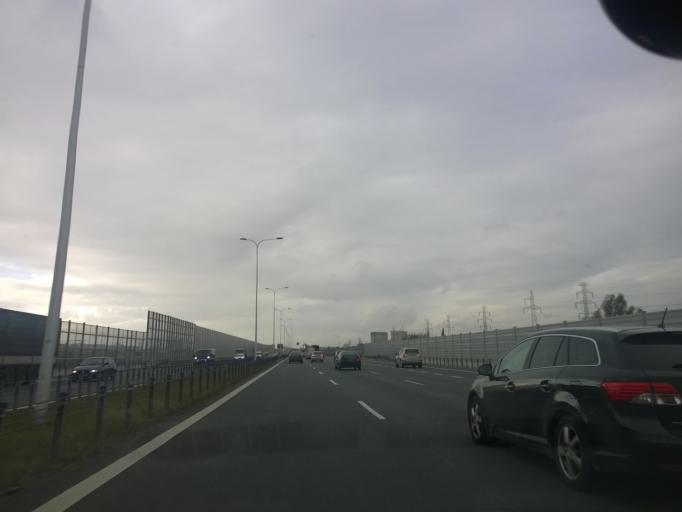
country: PL
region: Masovian Voivodeship
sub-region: Powiat pruszkowski
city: Michalowice
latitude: 52.1852
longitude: 20.8728
